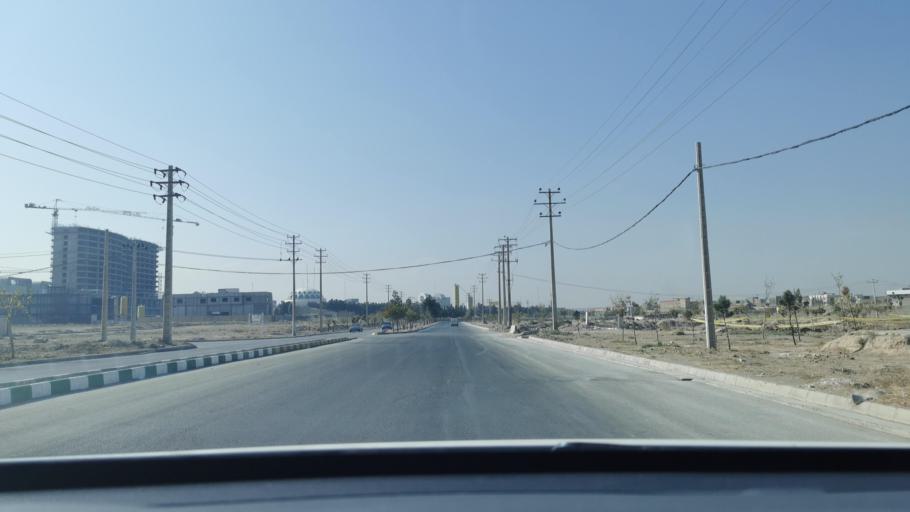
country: IR
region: Razavi Khorasan
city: Mashhad
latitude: 36.3480
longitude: 59.6074
